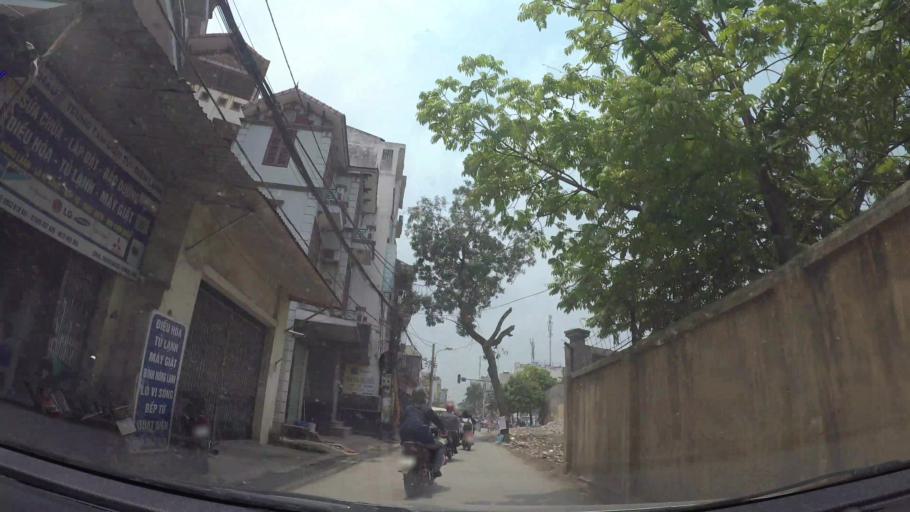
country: VN
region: Ha Noi
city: Tay Ho
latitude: 21.0769
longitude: 105.7878
